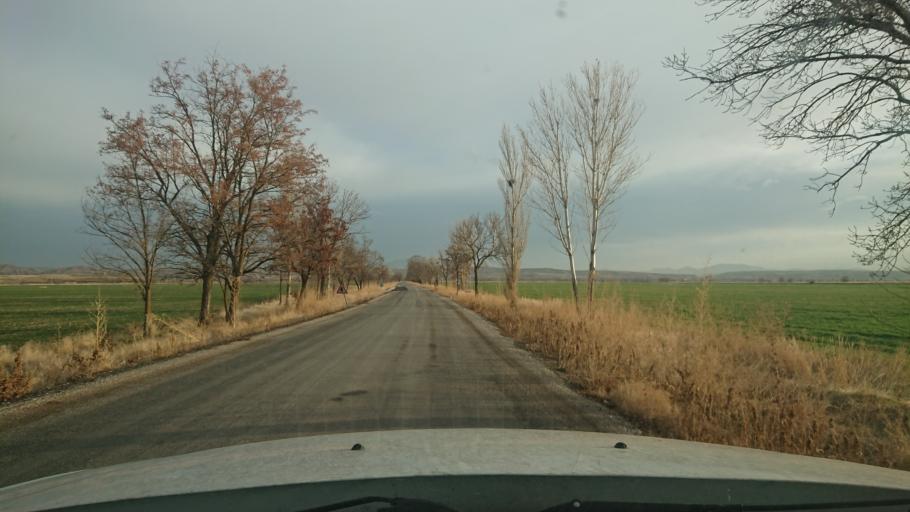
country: TR
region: Aksaray
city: Yesilova
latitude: 38.4618
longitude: 33.8410
